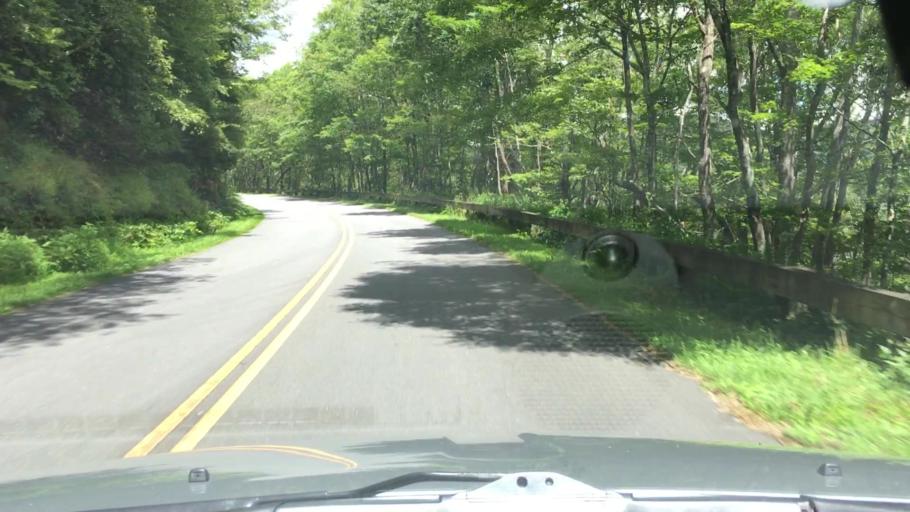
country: US
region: North Carolina
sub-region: Buncombe County
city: Swannanoa
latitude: 35.6877
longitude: -82.4095
